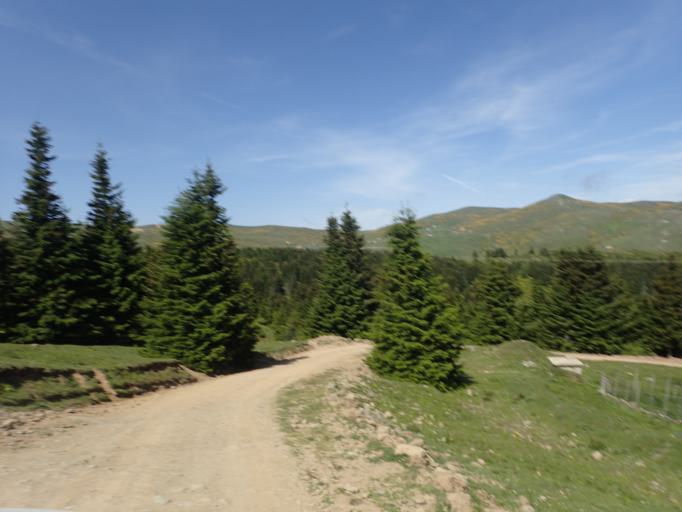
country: TR
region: Ordu
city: Topcam
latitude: 40.6393
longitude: 37.9521
